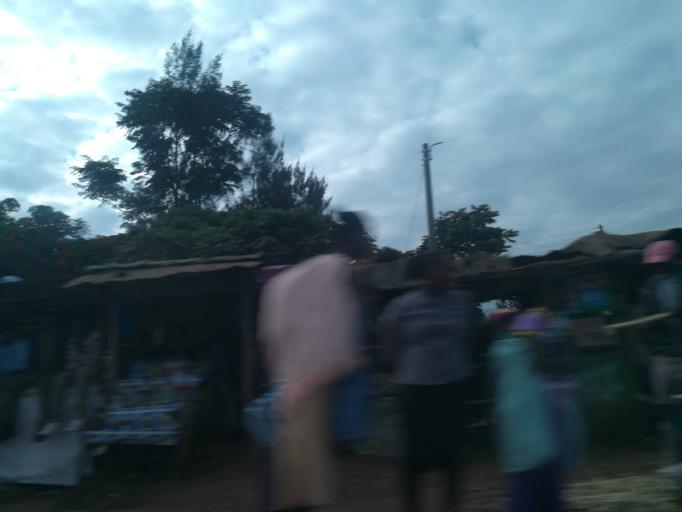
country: KE
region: Nairobi Area
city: Thika
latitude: -1.1303
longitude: 36.9822
